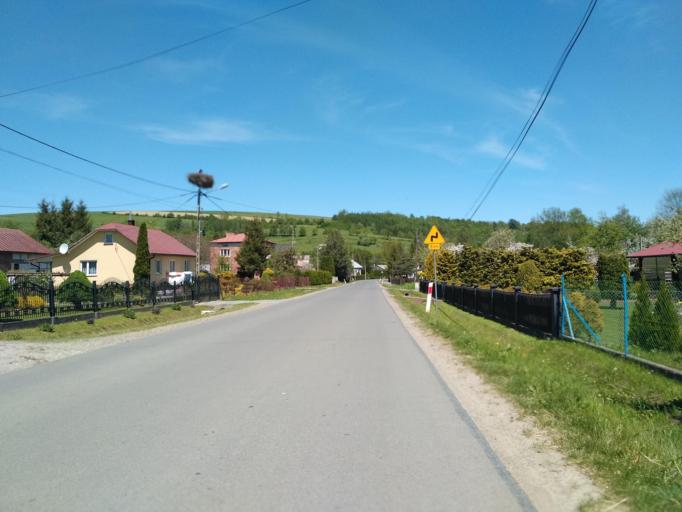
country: PL
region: Subcarpathian Voivodeship
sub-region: Powiat sanocki
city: Bukowsko
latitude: 49.5168
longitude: 22.0318
